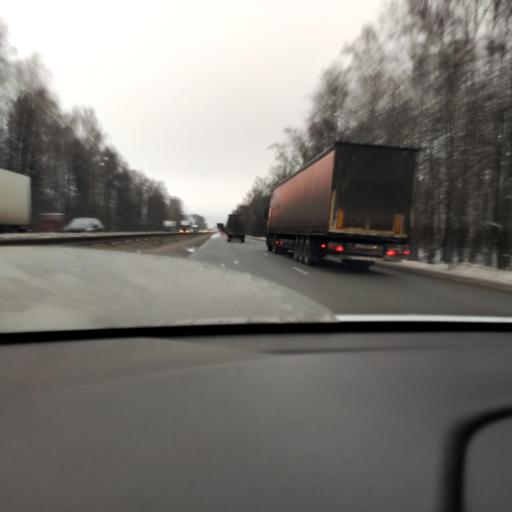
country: RU
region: Tatarstan
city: Osinovo
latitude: 55.8427
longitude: 48.8519
